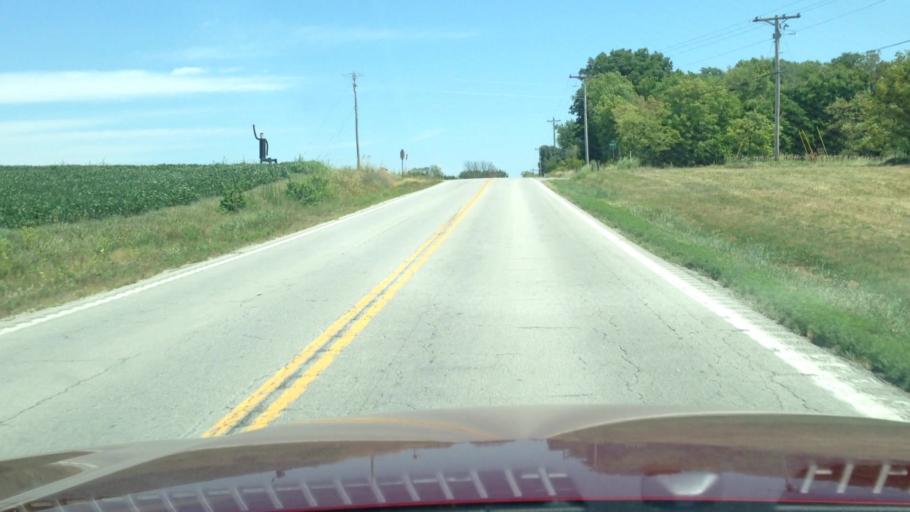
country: US
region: Missouri
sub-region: Clay County
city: Kearney
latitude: 39.3679
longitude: -94.4602
